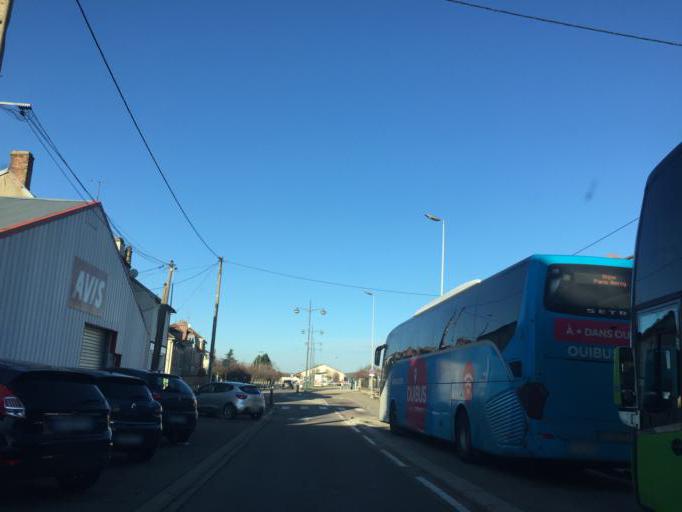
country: FR
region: Bourgogne
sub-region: Departement de l'Yonne
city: Auxerre
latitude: 47.7966
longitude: 3.5844
